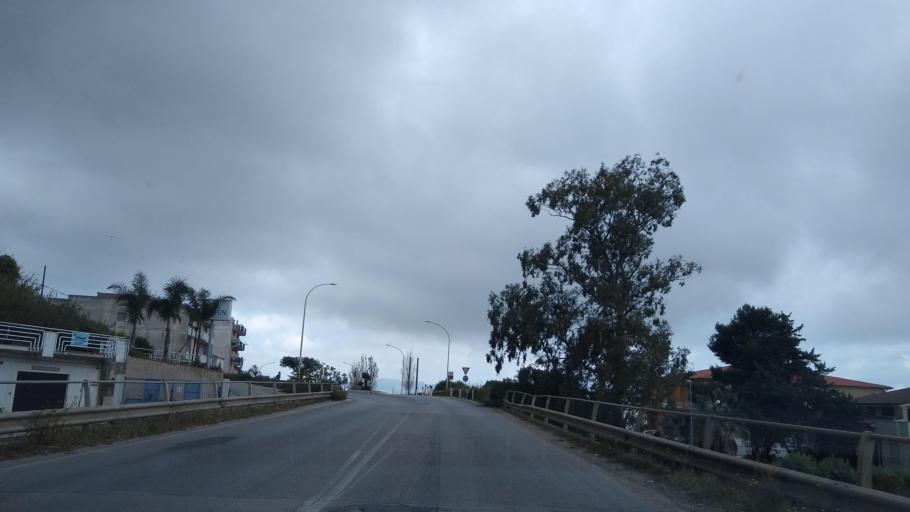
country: IT
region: Sicily
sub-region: Trapani
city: Alcamo
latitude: 37.9810
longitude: 12.9478
